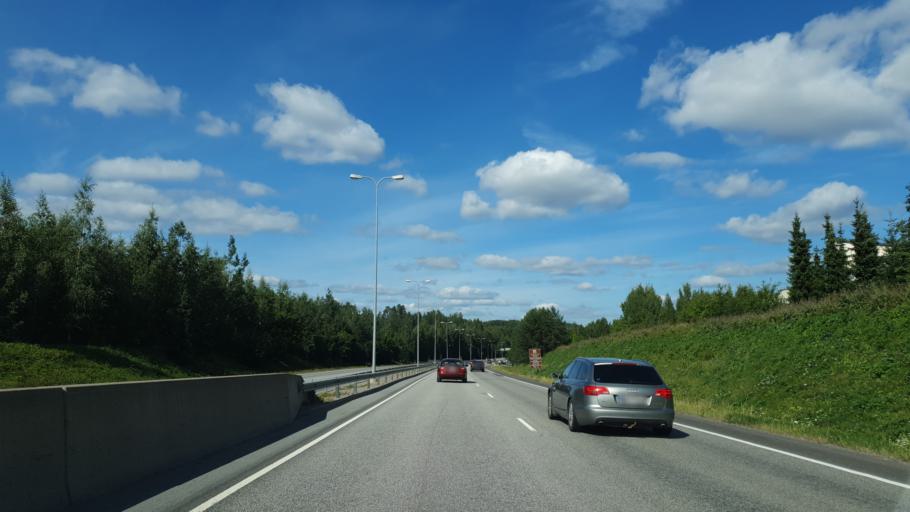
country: FI
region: Central Finland
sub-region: Jyvaeskylae
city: Jyvaeskylae
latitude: 62.2233
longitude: 25.7259
